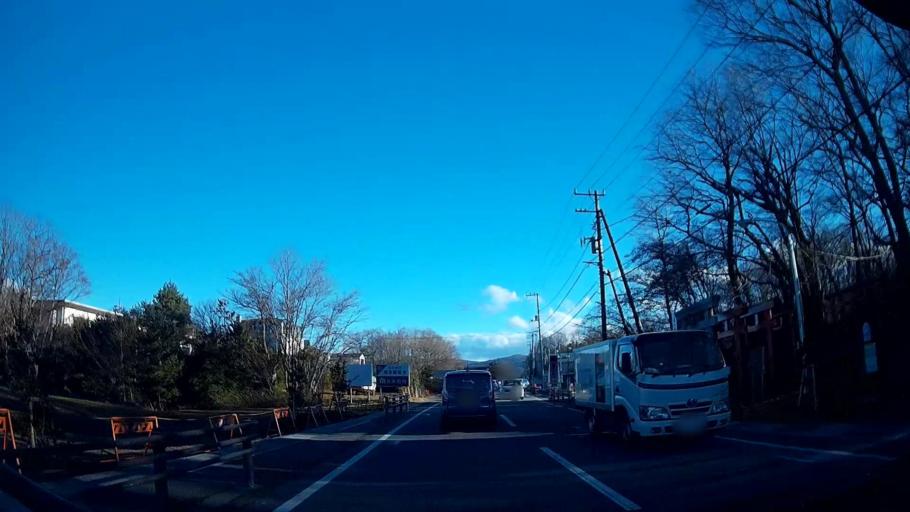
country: JP
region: Shizuoka
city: Gotemba
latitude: 35.4328
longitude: 138.8428
